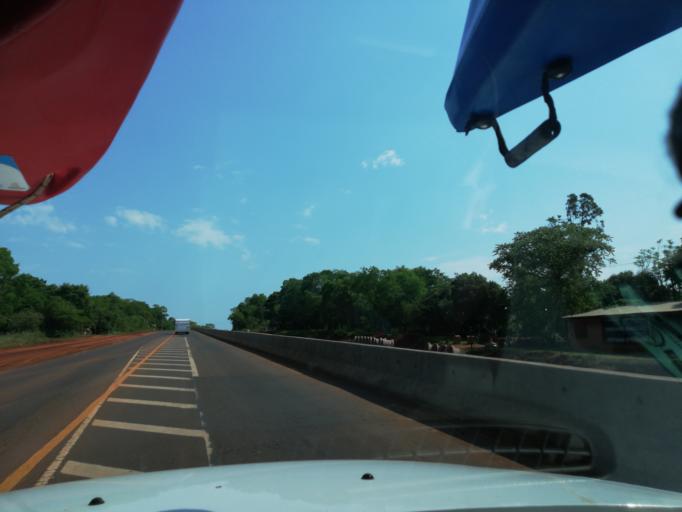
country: AR
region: Misiones
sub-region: Departamento de Candelaria
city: Loreto
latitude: -27.3476
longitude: -55.5473
